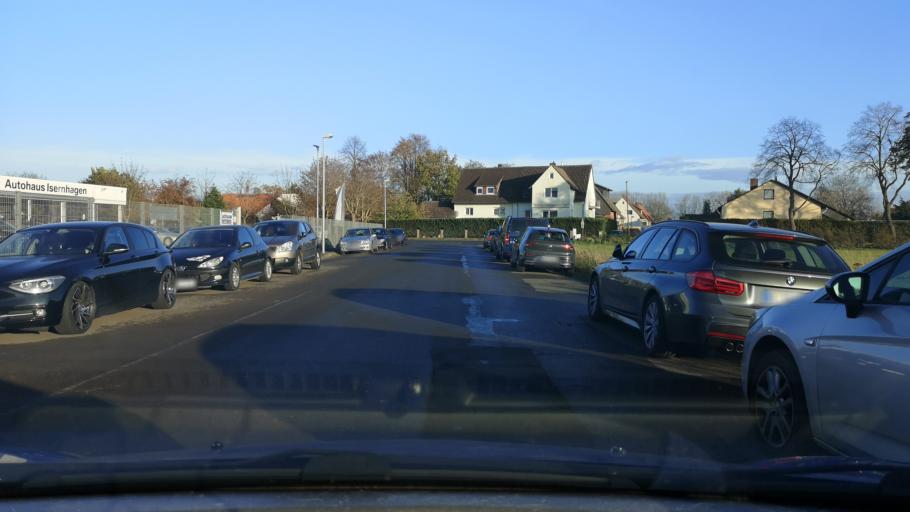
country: DE
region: Lower Saxony
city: Langenhagen
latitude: 52.4500
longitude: 9.7866
